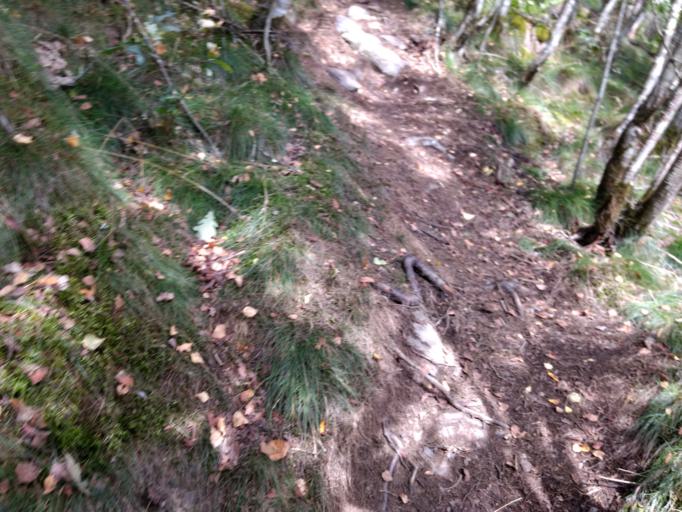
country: BE
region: Wallonia
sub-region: Province du Luxembourg
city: Houffalize
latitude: 50.1431
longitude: 5.7336
